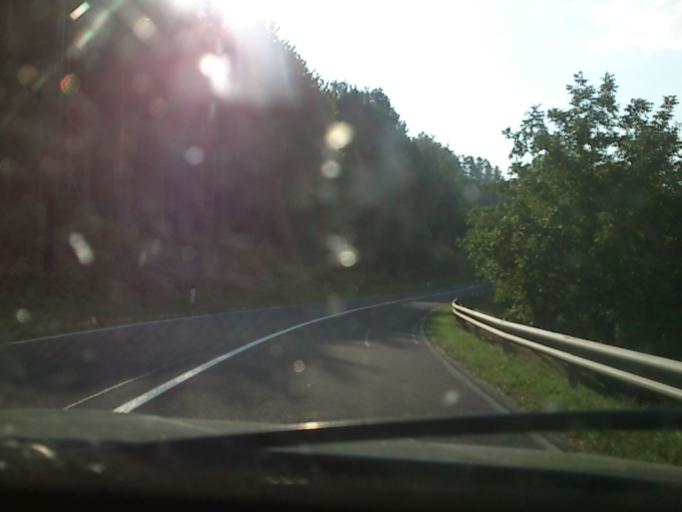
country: SI
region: Starse
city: Starse
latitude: 46.4953
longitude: 15.7893
